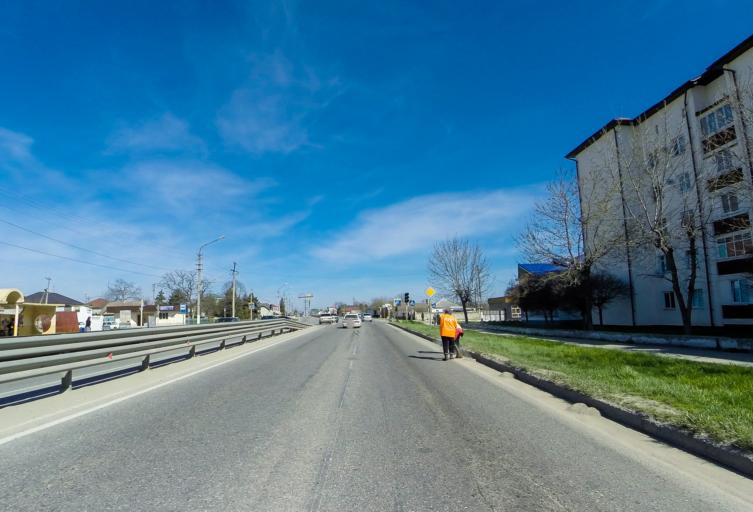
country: RU
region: Kabardino-Balkariya
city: Chegem Vtoroy
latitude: 43.5664
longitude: 43.5899
